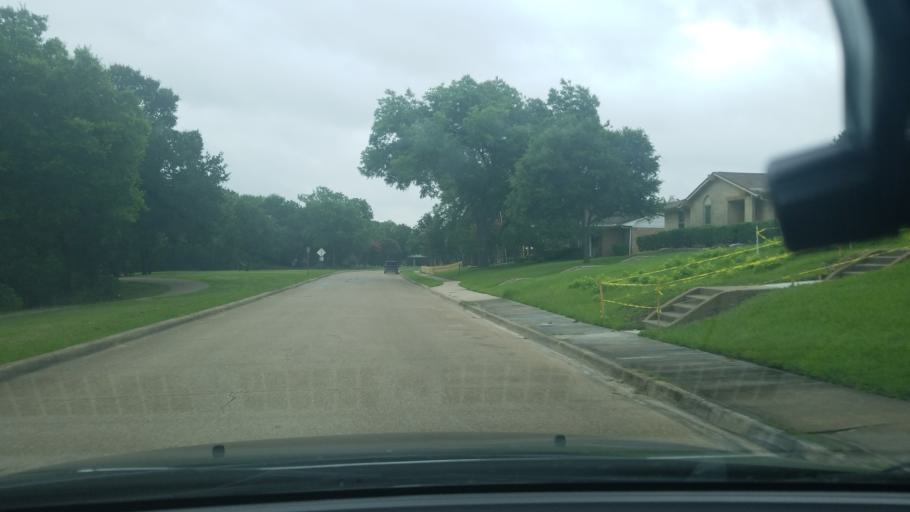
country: US
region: Texas
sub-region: Dallas County
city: Mesquite
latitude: 32.7821
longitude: -96.6322
